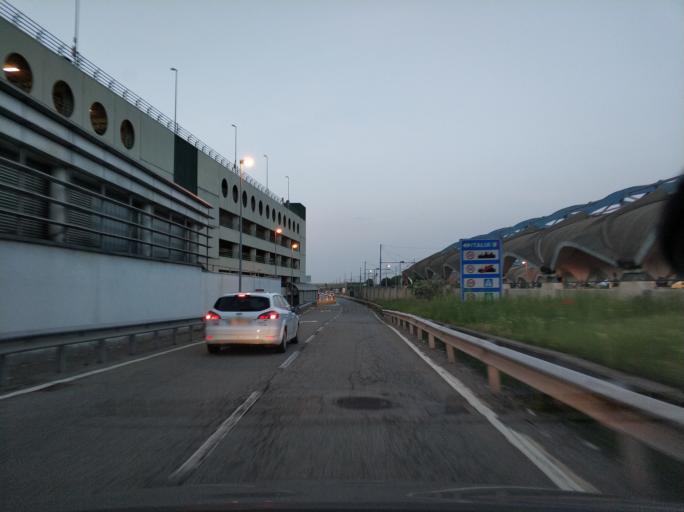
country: IT
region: Piedmont
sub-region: Provincia di Torino
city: Caselle Torinese
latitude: 45.1917
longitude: 7.6419
